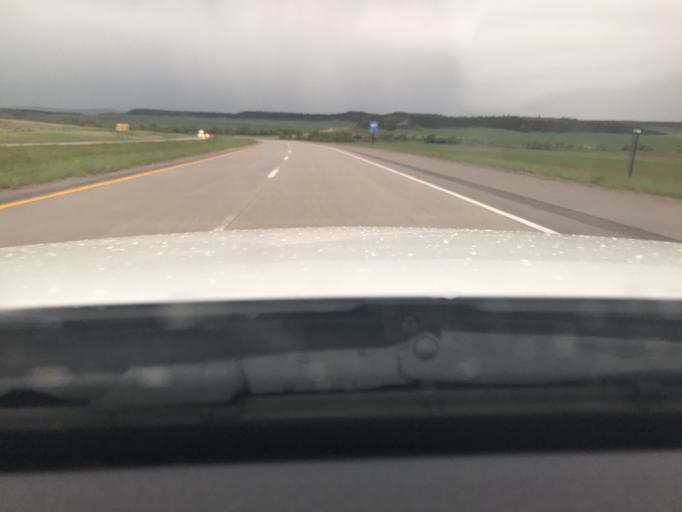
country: US
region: Wyoming
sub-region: Platte County
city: Guernsey
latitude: 42.4861
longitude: -105.0332
